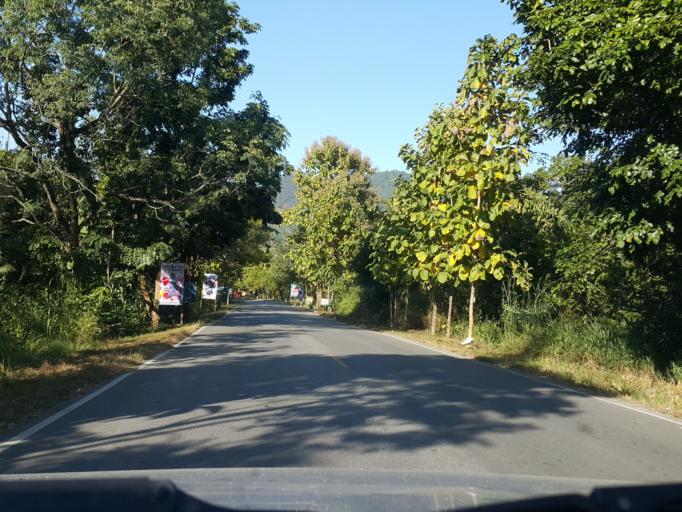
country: TH
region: Mae Hong Son
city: Mae Hi
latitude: 19.3089
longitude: 98.4527
